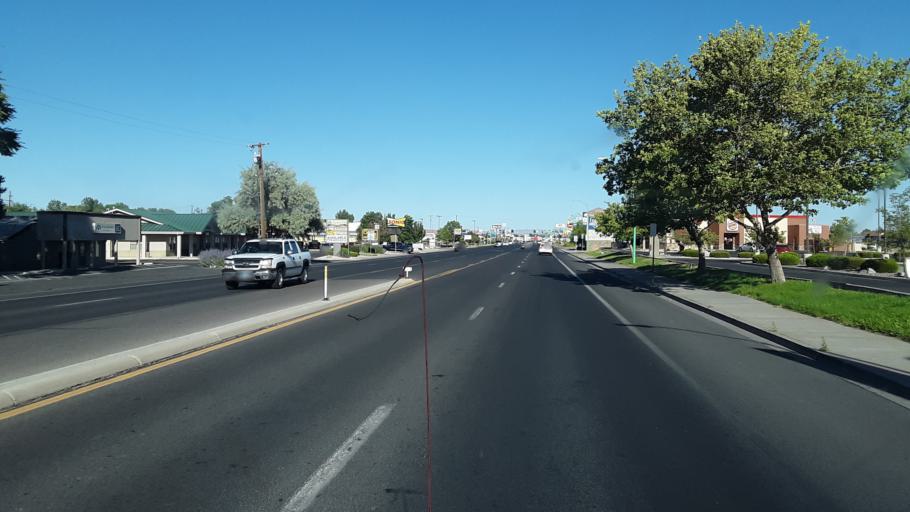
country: US
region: Nevada
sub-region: Churchill County
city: Fallon
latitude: 39.4772
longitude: -118.8042
